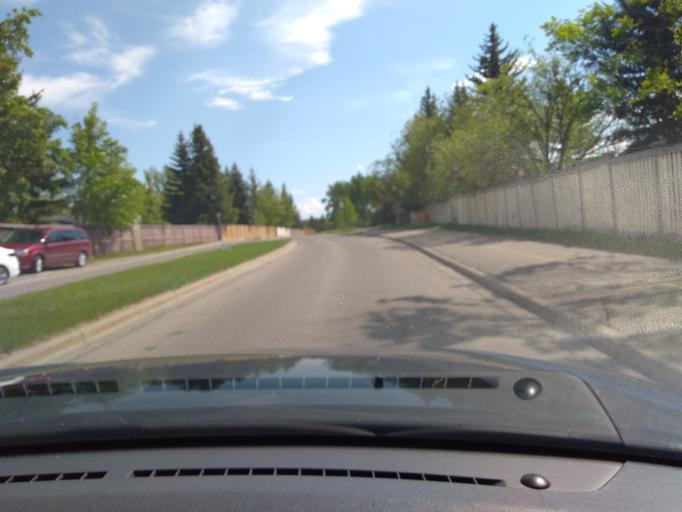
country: CA
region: Alberta
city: Calgary
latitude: 50.9355
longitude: -114.1181
